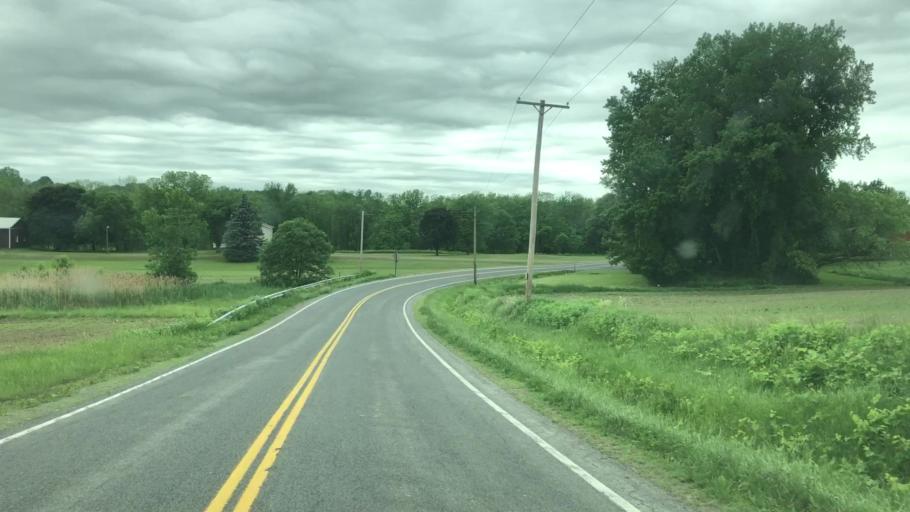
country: US
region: New York
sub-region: Wayne County
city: Macedon
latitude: 43.1163
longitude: -77.2855
